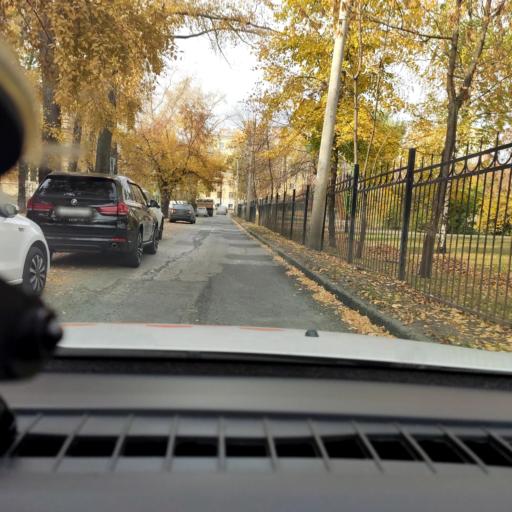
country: RU
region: Samara
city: Samara
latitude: 53.2007
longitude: 50.2208
